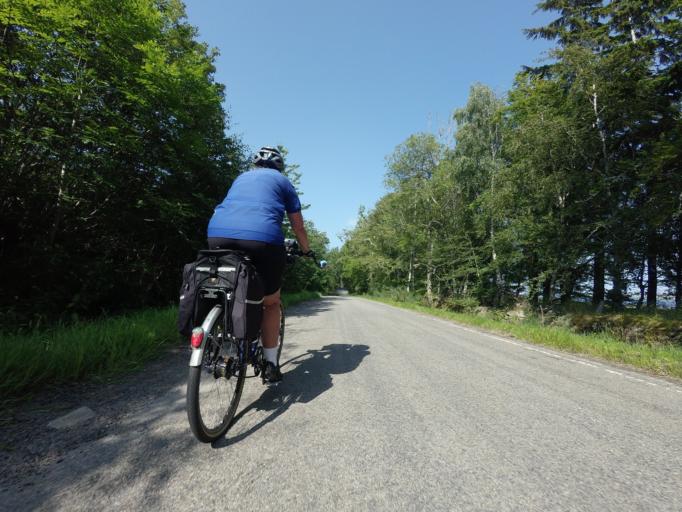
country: GB
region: Scotland
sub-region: Highland
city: Evanton
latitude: 57.6464
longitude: -4.3528
